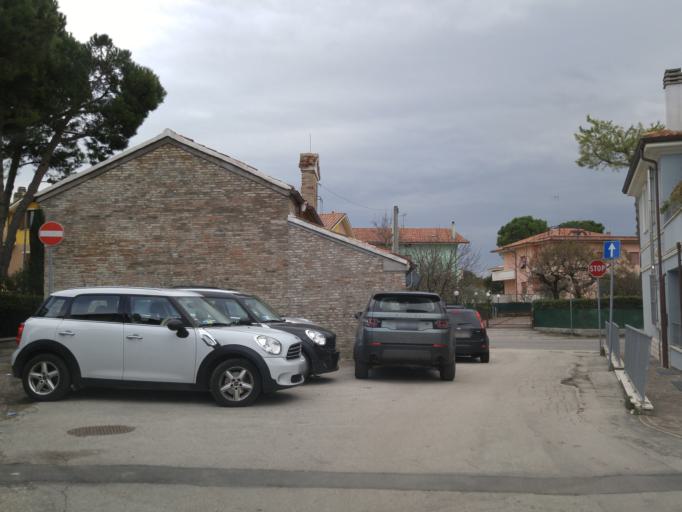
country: IT
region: The Marches
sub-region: Provincia di Pesaro e Urbino
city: Centinarola
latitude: 43.8414
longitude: 12.9983
